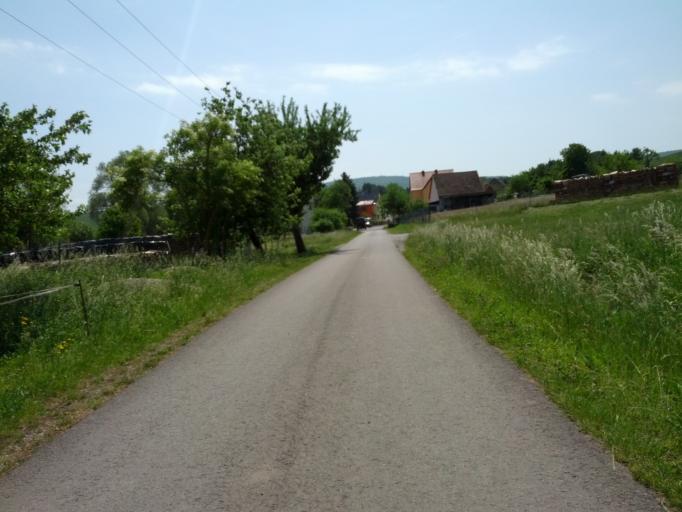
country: DE
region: Thuringia
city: Wiesenthal
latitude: 50.7092
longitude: 10.1706
